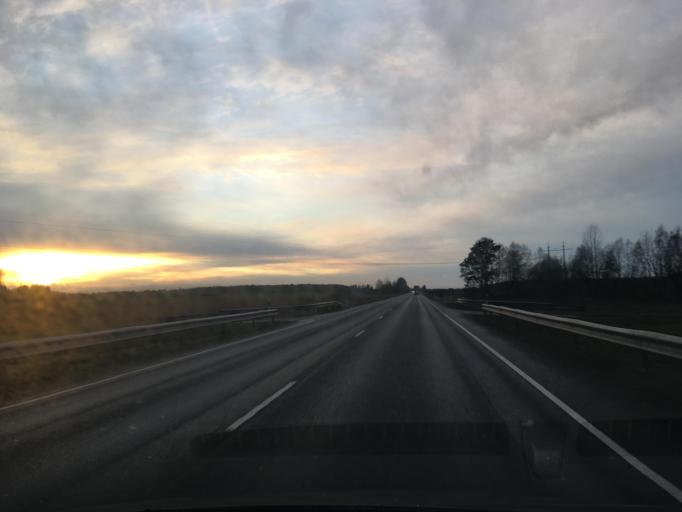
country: EE
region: Laeaene-Virumaa
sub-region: Someru vald
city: Someru
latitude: 59.3688
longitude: 26.5372
